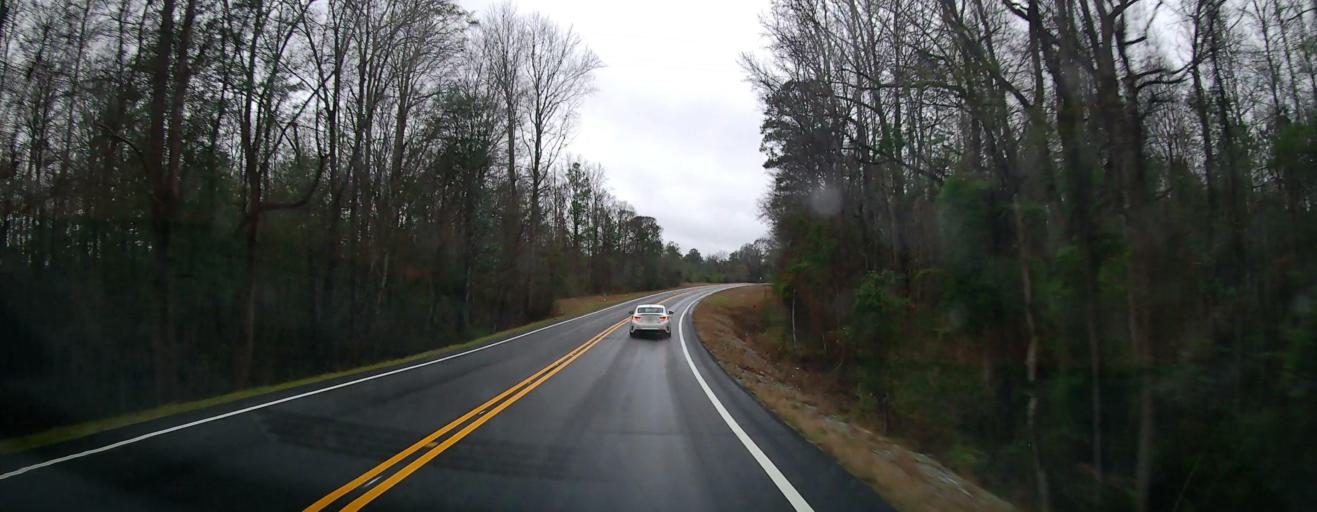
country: US
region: Alabama
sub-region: Chilton County
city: Clanton
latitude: 32.6720
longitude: -86.7862
